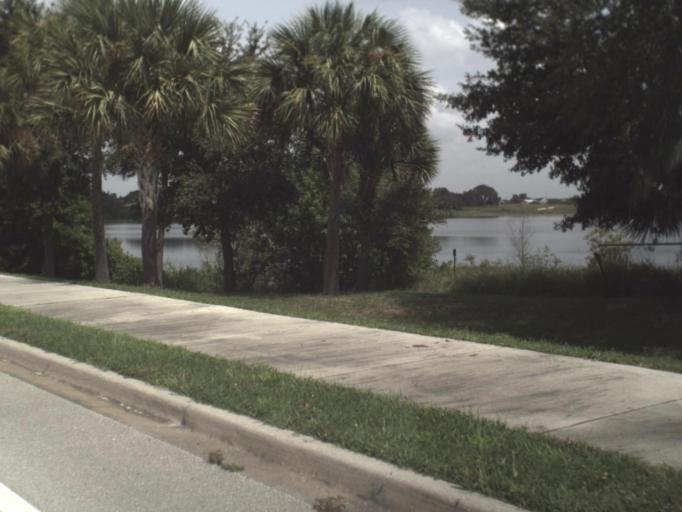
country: US
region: Florida
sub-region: Highlands County
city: Avon Park
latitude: 27.5785
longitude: -81.5143
